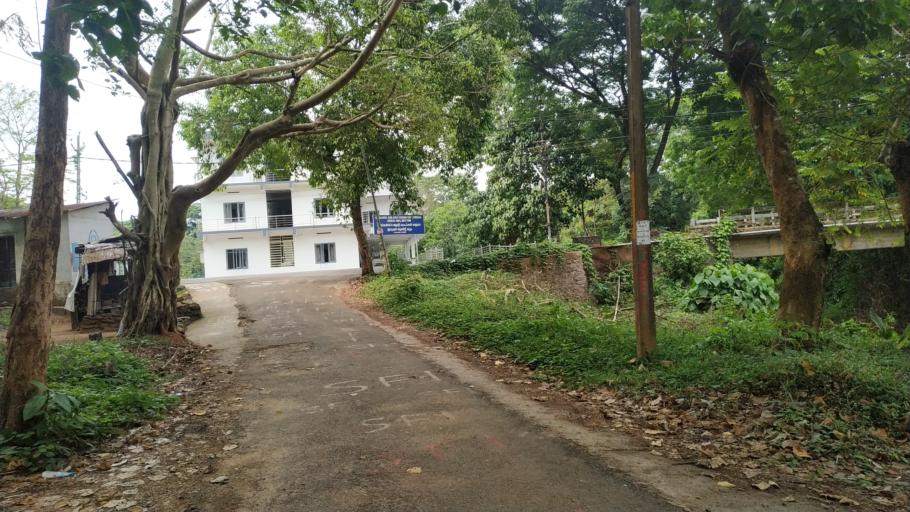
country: IN
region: Kerala
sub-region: Kottayam
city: Lalam
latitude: 9.8436
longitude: 76.7403
